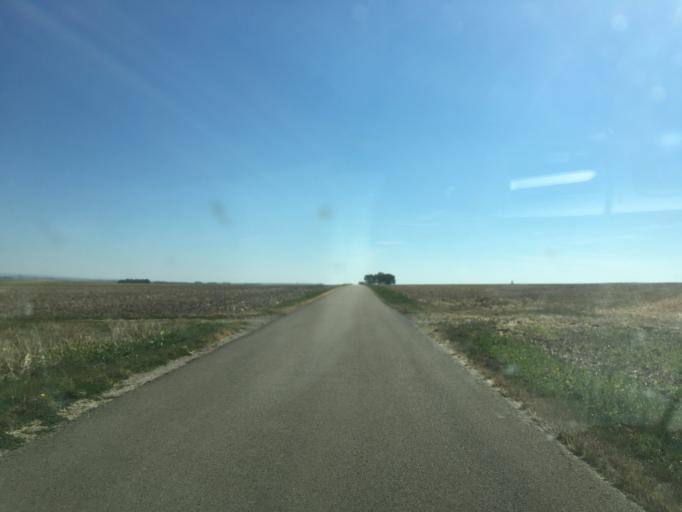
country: FR
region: Bourgogne
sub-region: Departement de l'Yonne
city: Aillant-sur-Tholon
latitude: 47.9164
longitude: 3.3831
